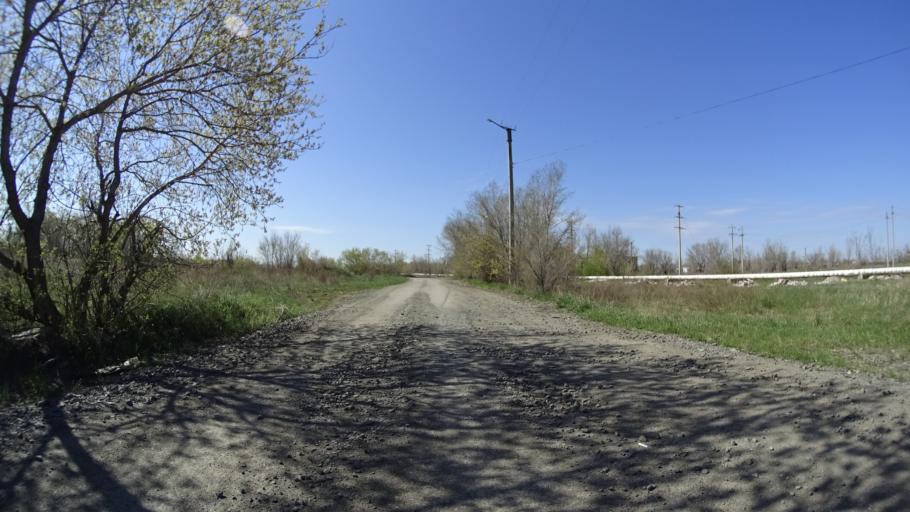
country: RU
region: Chelyabinsk
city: Troitsk
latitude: 54.1396
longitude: 61.5670
